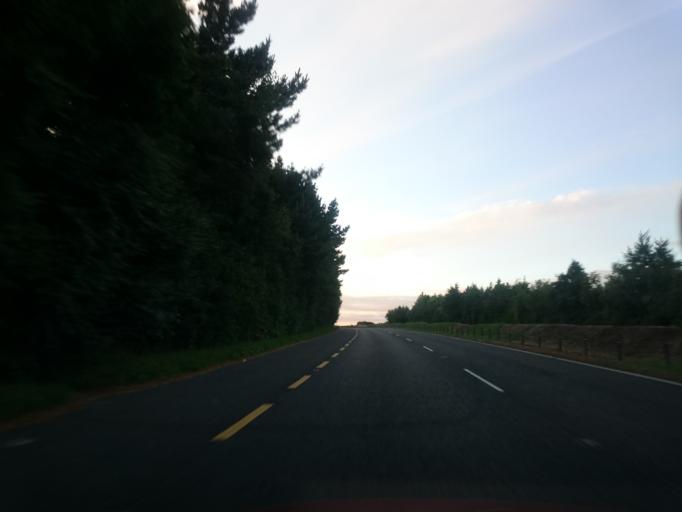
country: IE
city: Kilquade
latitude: 53.0821
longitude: -6.0895
